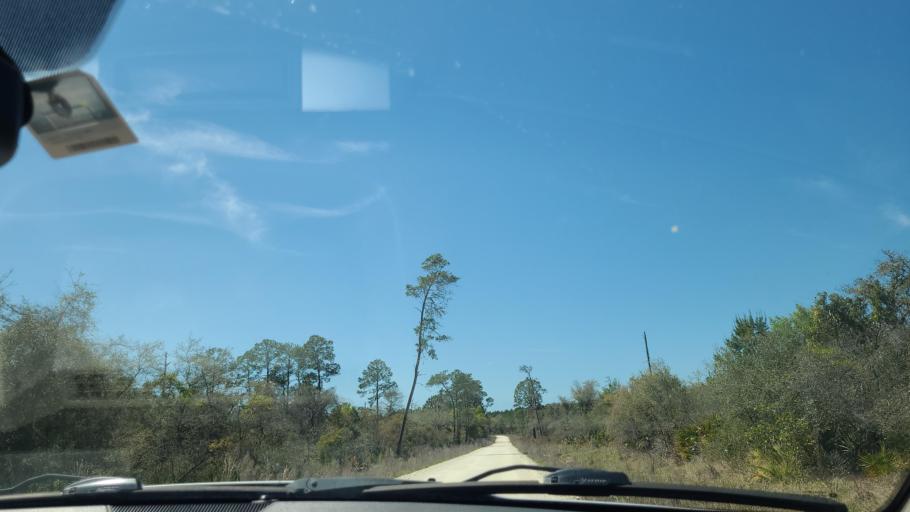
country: US
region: Florida
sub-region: Putnam County
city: Interlachen
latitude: 29.4393
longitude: -81.7672
